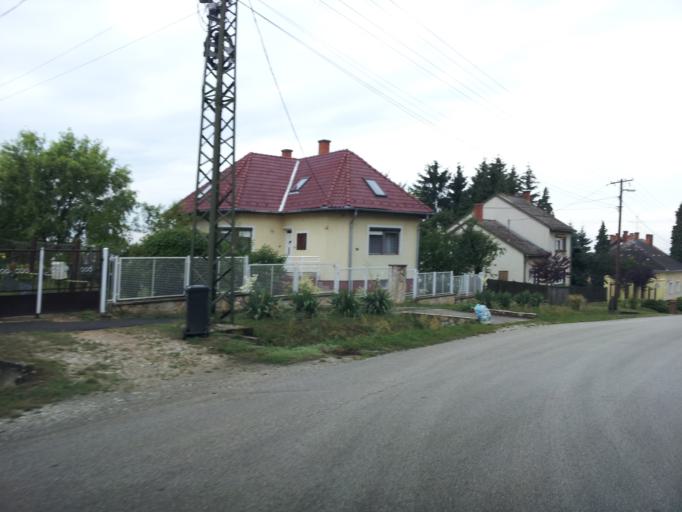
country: HU
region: Vas
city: Kormend
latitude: 46.9644
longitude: 16.6126
